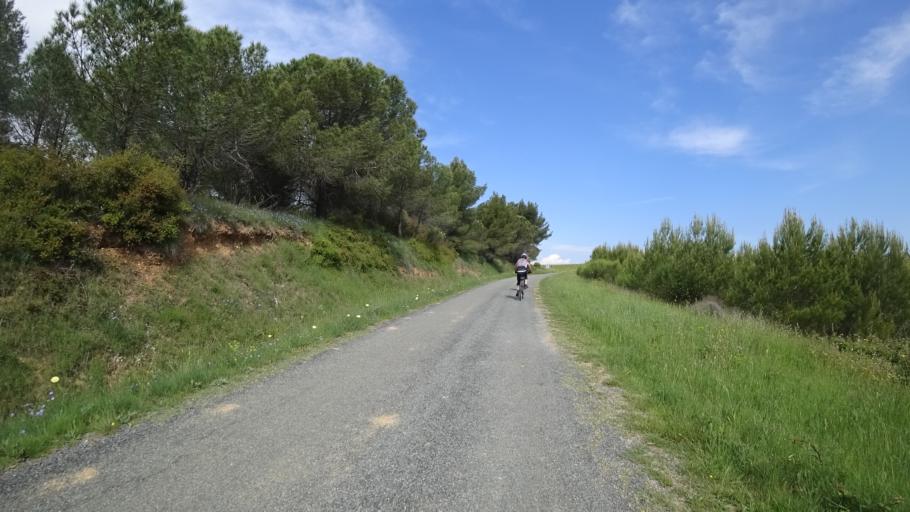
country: FR
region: Languedoc-Roussillon
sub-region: Departement de l'Aude
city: Canet
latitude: 43.2569
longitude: 2.8064
